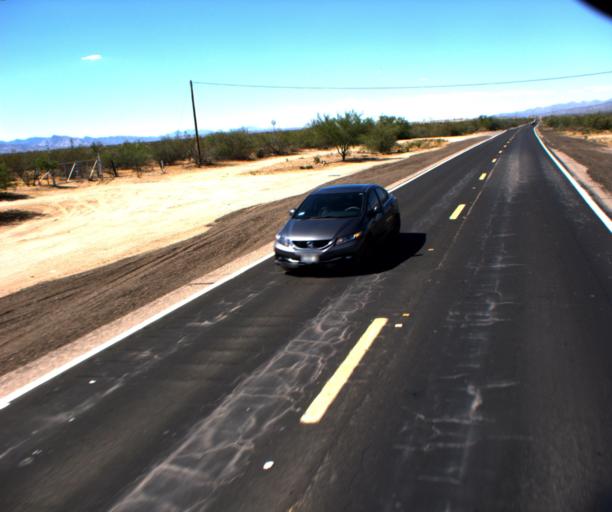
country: US
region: Arizona
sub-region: Yavapai County
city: Bagdad
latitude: 34.7193
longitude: -113.6148
